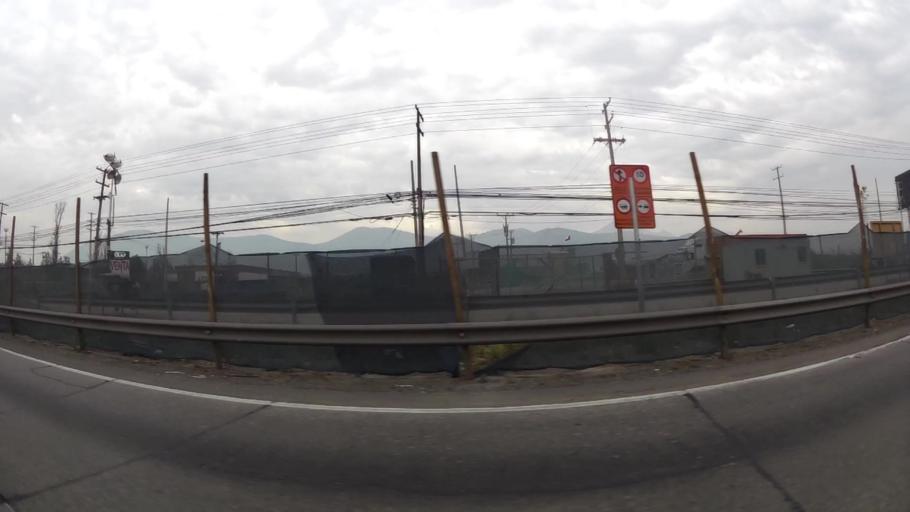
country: CL
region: Santiago Metropolitan
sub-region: Provincia de Chacabuco
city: Chicureo Abajo
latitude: -33.3462
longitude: -70.7093
